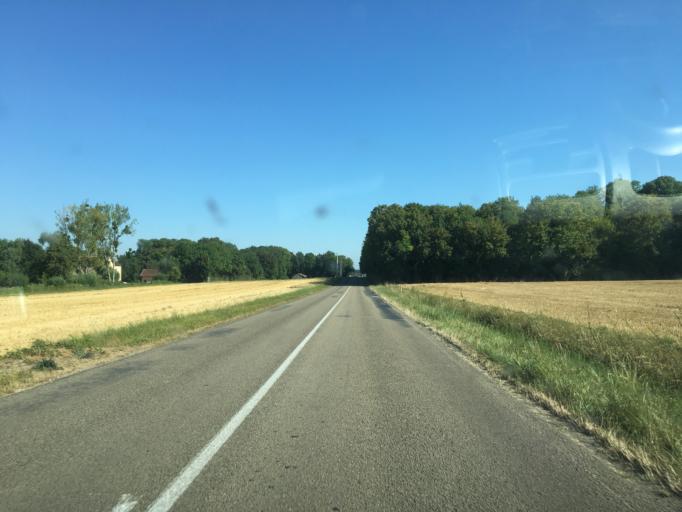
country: FR
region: Bourgogne
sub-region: Departement de l'Yonne
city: Aillant-sur-Tholon
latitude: 47.9022
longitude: 3.3565
